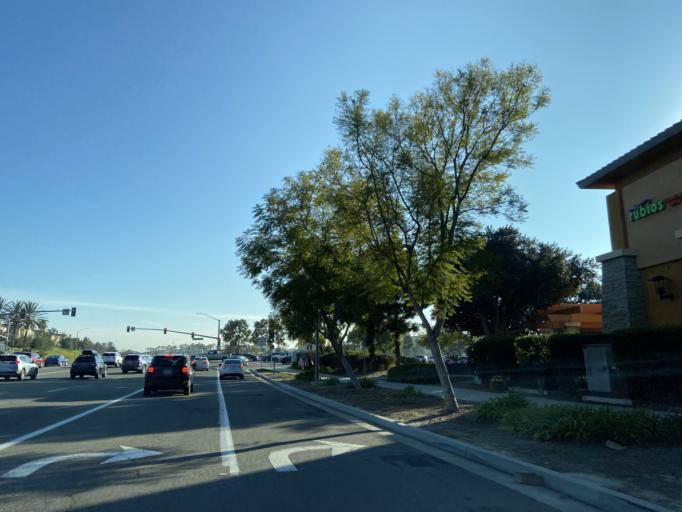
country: US
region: California
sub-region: San Diego County
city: Bonita
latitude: 32.6286
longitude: -116.9647
